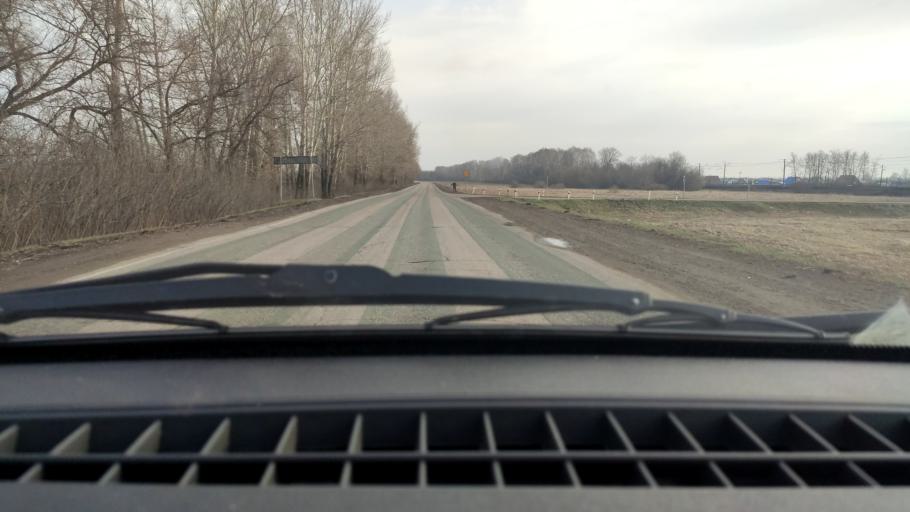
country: RU
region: Bashkortostan
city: Chishmy
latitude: 54.4497
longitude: 55.2470
